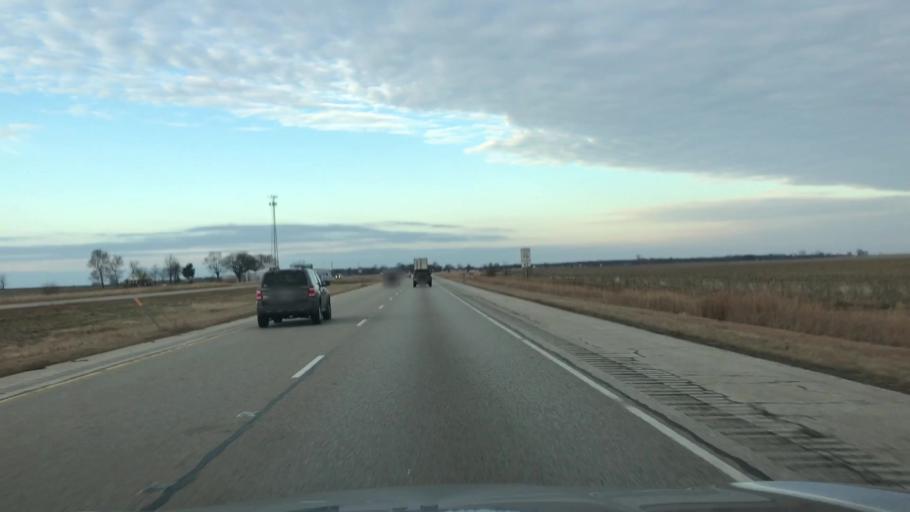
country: US
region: Illinois
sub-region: Logan County
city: Atlanta
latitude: 40.3203
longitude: -89.1576
